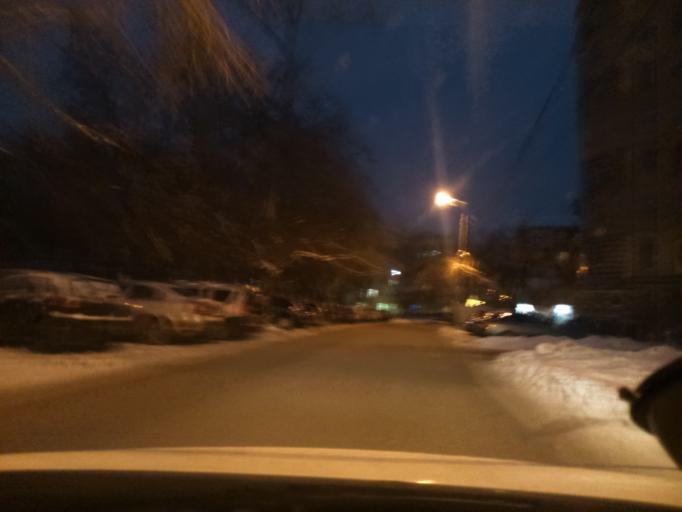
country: RU
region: Perm
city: Perm
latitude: 57.9868
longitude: 56.2468
